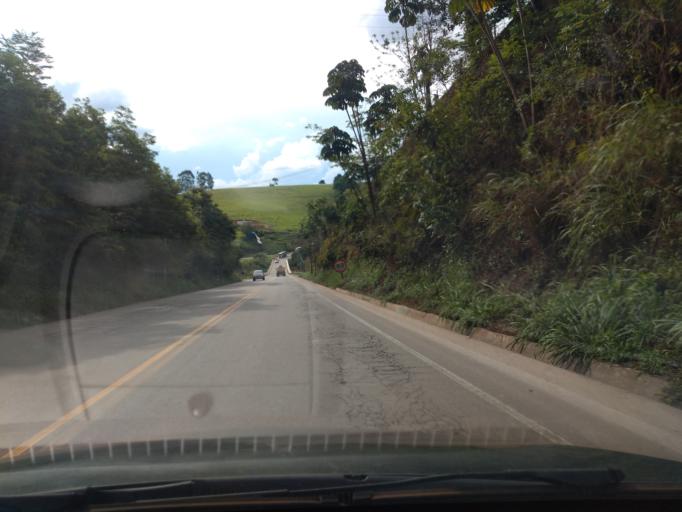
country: BR
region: Minas Gerais
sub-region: Varginha
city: Varginha
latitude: -21.6127
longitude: -45.4282
